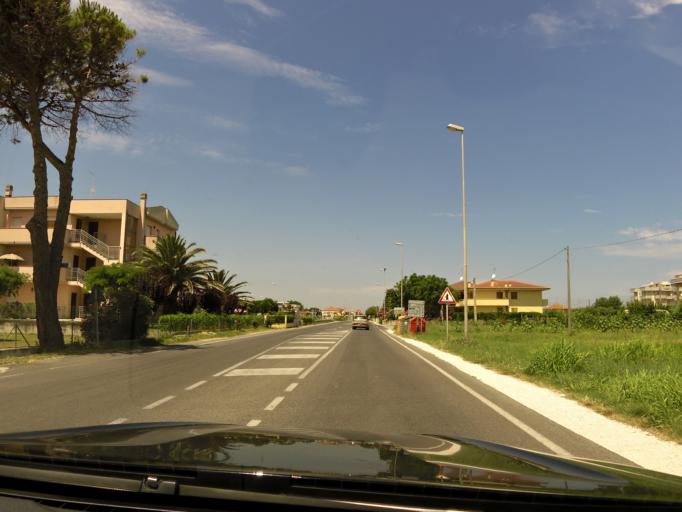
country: IT
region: The Marches
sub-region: Provincia di Pesaro e Urbino
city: Marotta
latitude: 43.7822
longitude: 13.1173
